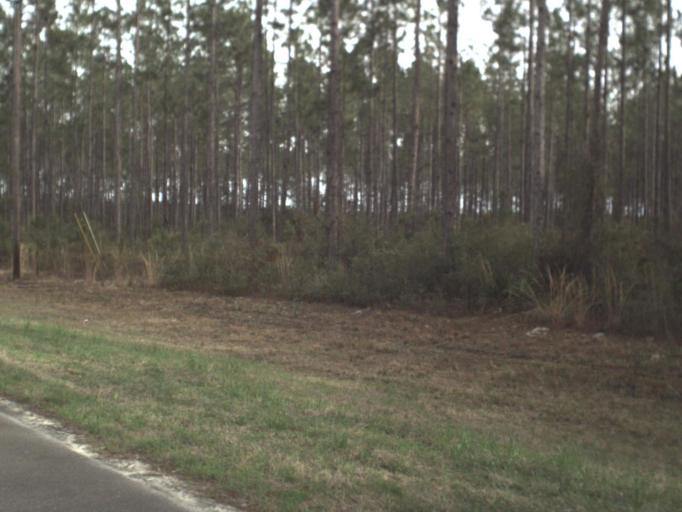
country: US
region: Florida
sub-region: Gulf County
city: Wewahitchka
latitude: 30.1330
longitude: -85.3506
